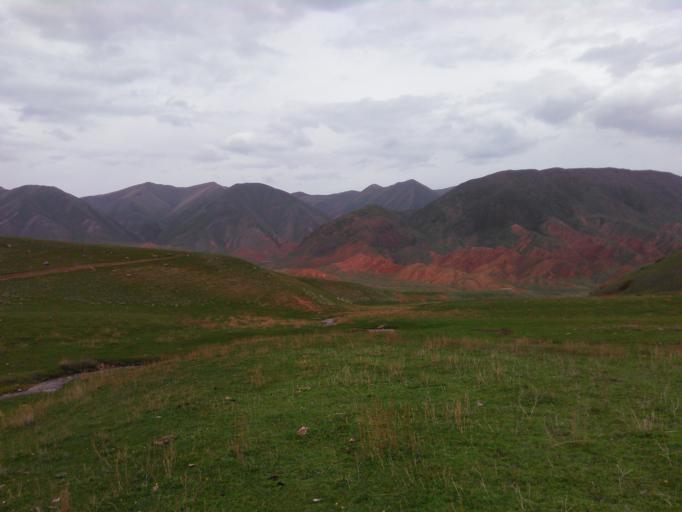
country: KG
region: Chuy
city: Bystrovka
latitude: 42.5552
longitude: 75.6110
